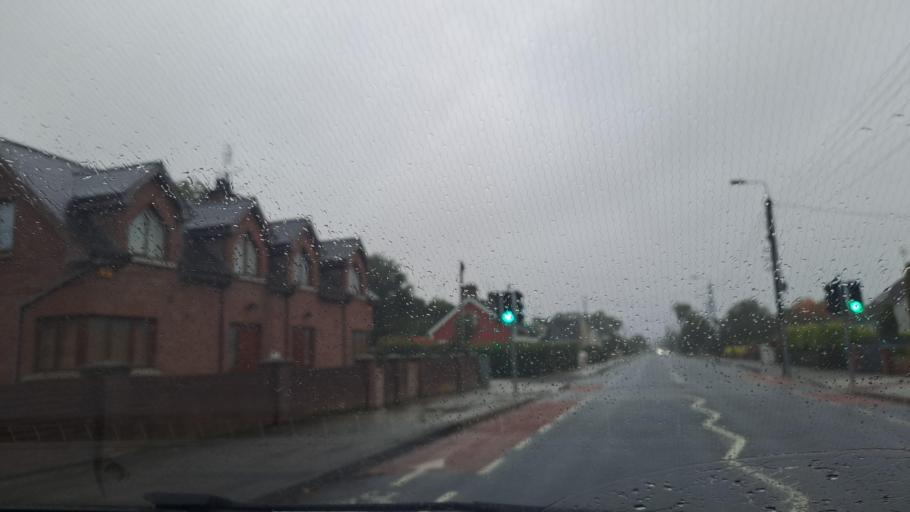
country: IE
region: Leinster
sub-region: Lu
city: Dundalk
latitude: 53.9944
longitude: -6.3847
